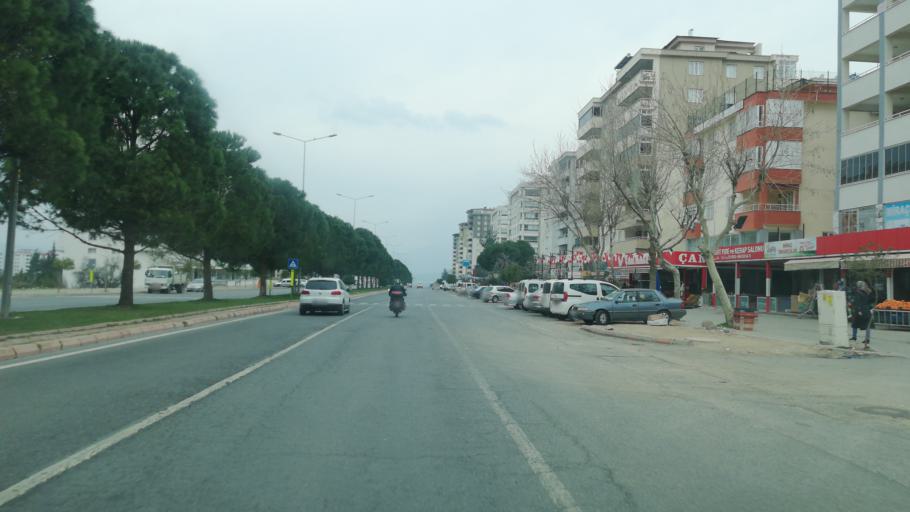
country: TR
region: Kahramanmaras
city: Kahramanmaras
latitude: 37.6001
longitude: 36.8300
